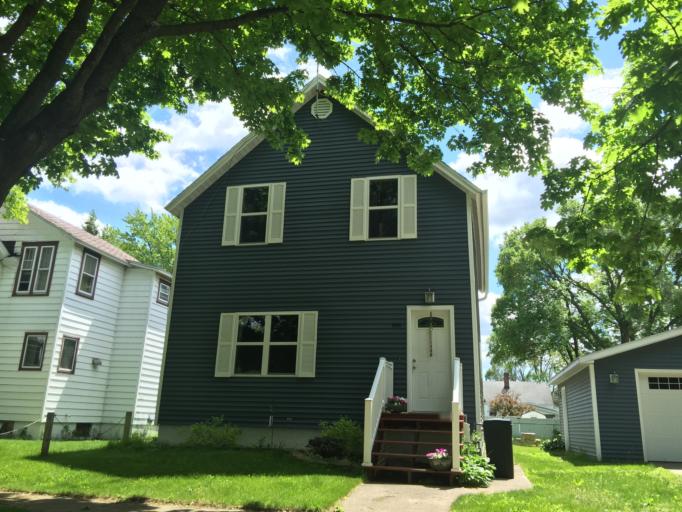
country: US
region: Wisconsin
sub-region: Marinette County
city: Marinette
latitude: 45.1107
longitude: -87.6270
